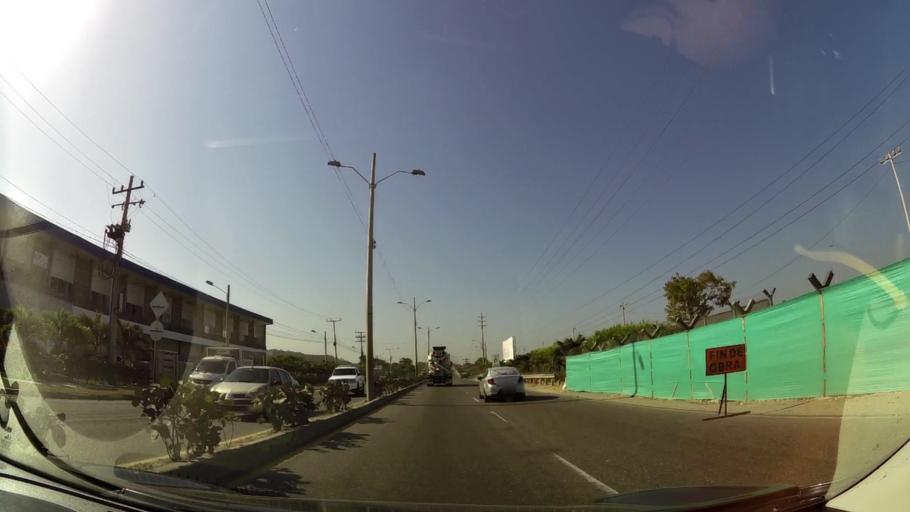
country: CO
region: Bolivar
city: Cartagena
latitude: 10.3756
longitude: -75.5043
